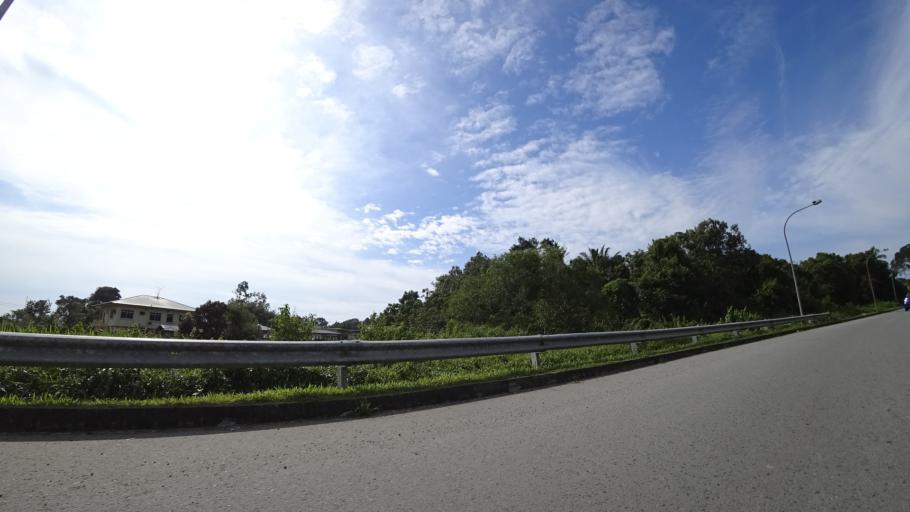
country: BN
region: Brunei and Muara
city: Bandar Seri Begawan
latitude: 4.8708
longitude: 114.8079
